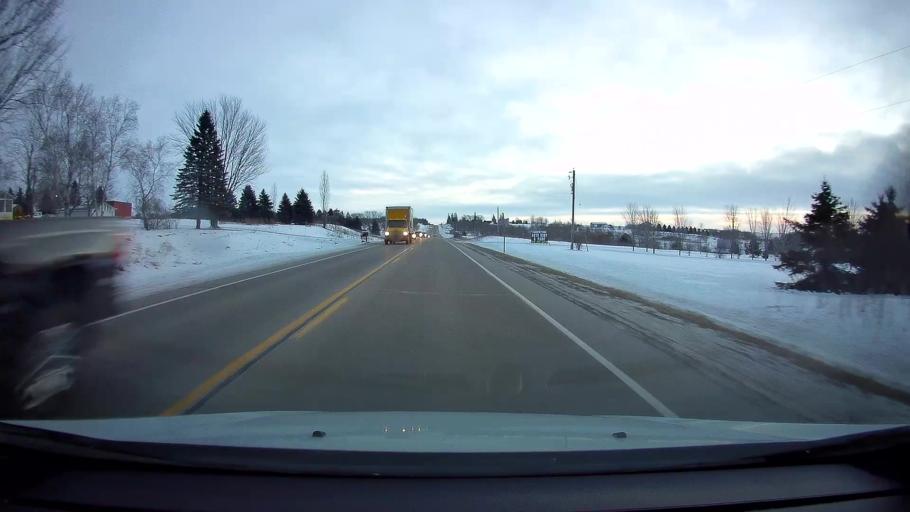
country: US
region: Wisconsin
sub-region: Saint Croix County
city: New Richmond
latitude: 45.1371
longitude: -92.5079
